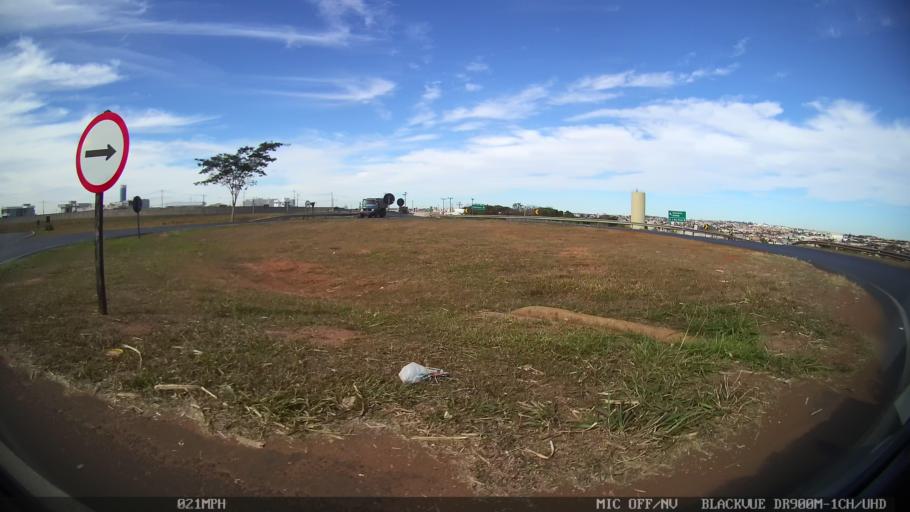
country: BR
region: Sao Paulo
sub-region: Catanduva
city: Catanduva
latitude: -21.1149
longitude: -48.9796
